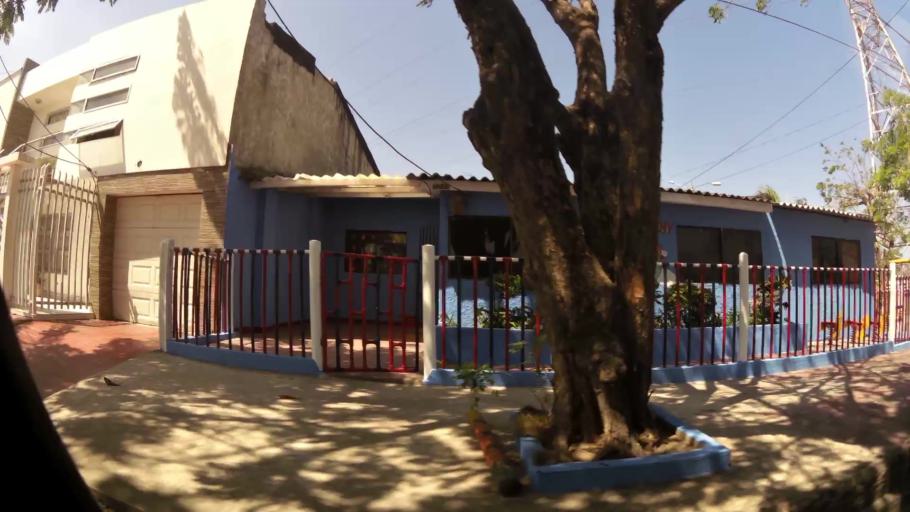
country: CO
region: Atlantico
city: Barranquilla
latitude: 10.9817
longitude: -74.8185
